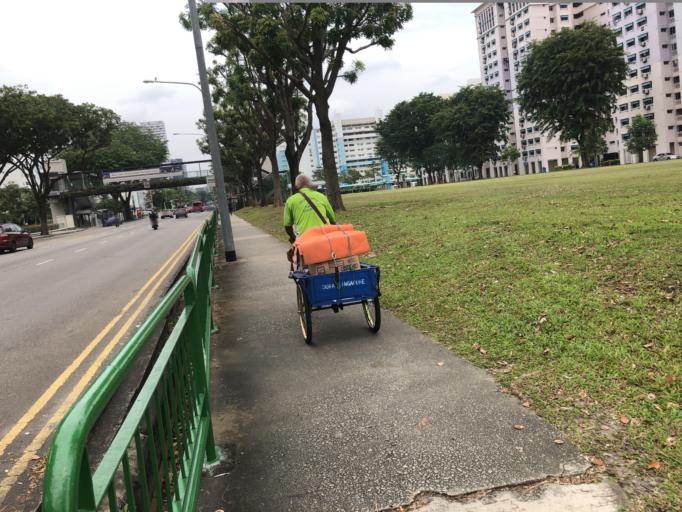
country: SG
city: Singapore
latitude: 1.3166
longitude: 103.8594
